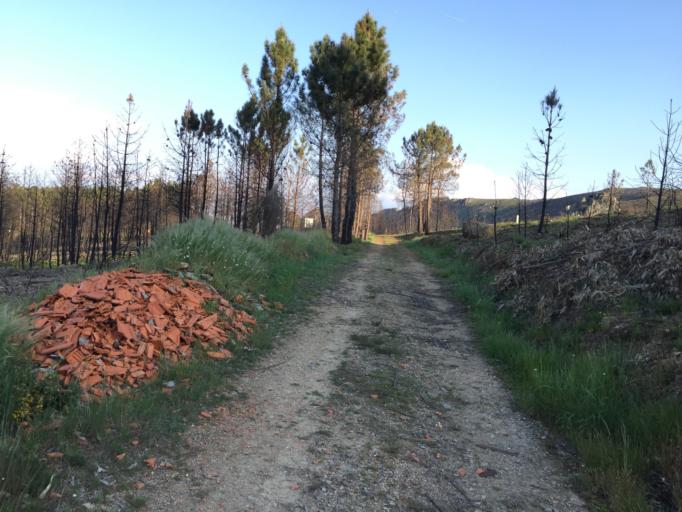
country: PT
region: Coimbra
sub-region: Pampilhosa da Serra
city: Pampilhosa da Serra
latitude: 40.1099
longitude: -7.8731
